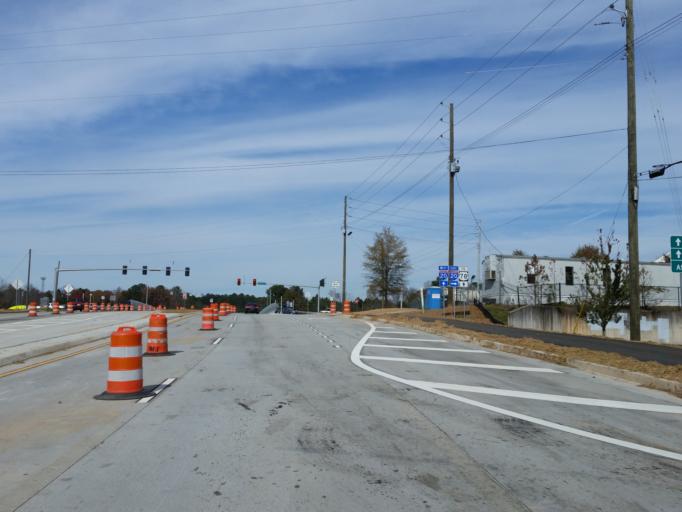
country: US
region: Georgia
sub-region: Douglas County
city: Lithia Springs
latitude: 33.7667
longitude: -84.6513
